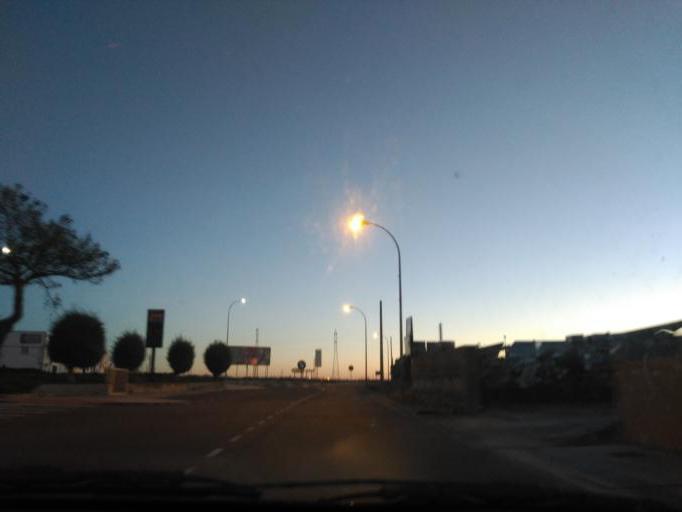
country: ES
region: Castille and Leon
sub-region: Provincia de Salamanca
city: Villares de la Reina
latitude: 41.0049
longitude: -5.6496
